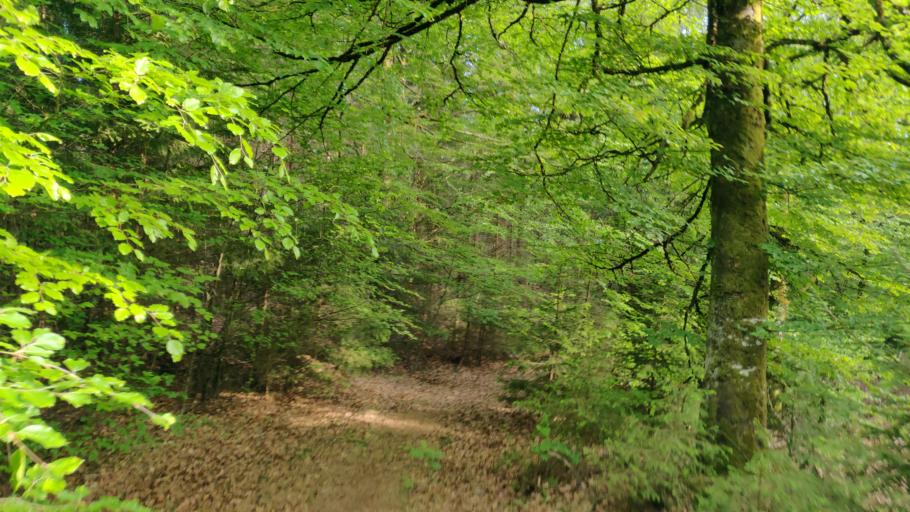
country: SE
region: Vaestra Goetaland
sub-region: Ulricehamns Kommun
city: Ulricehamn
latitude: 57.7841
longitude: 13.3723
